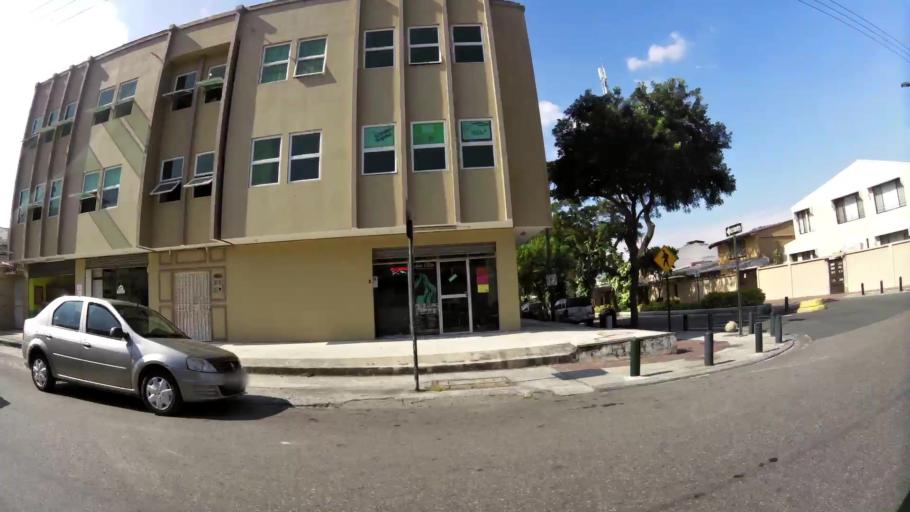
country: EC
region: Guayas
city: Guayaquil
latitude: -2.1678
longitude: -79.9410
